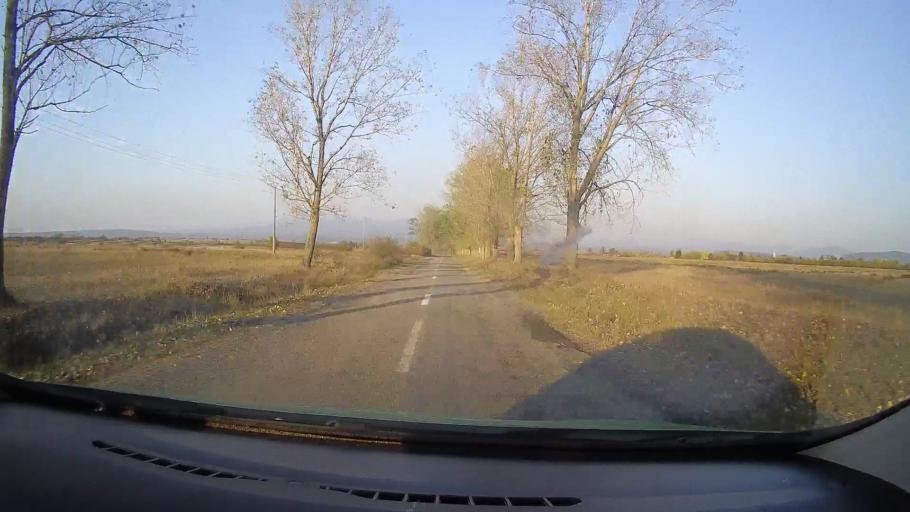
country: RO
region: Arad
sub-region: Comuna Barsa
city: Barsa
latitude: 46.3810
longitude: 22.0589
